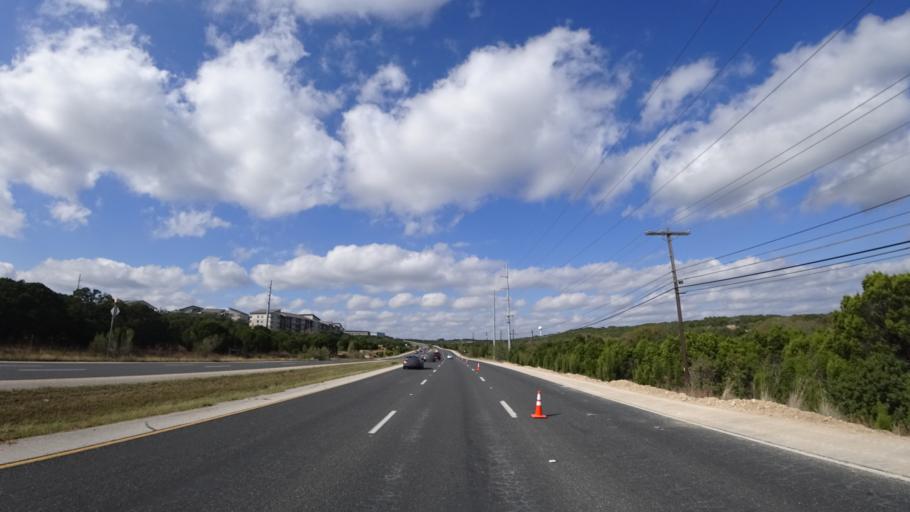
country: US
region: Texas
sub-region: Travis County
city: Barton Creek
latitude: 30.2491
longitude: -97.8517
